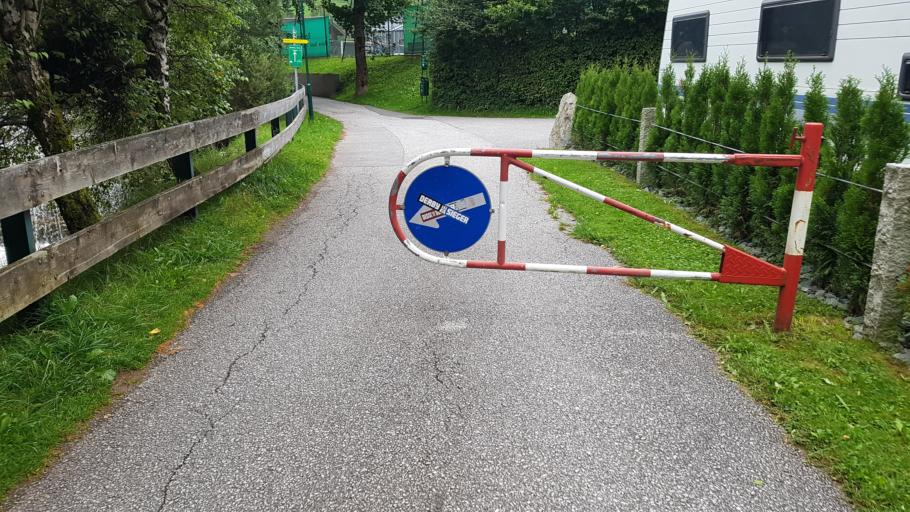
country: AT
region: Salzburg
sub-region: Politischer Bezirk Zell am See
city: Leogang
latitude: 47.4407
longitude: 12.7583
